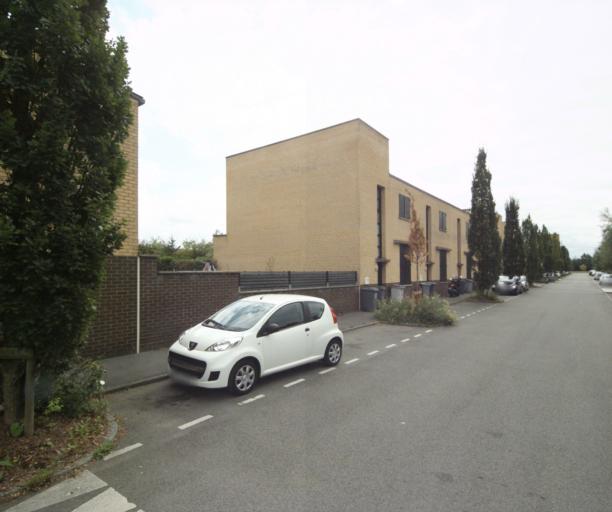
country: FR
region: Nord-Pas-de-Calais
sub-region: Departement du Nord
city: Villeneuve-d'Ascq
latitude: 50.6097
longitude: 3.1611
